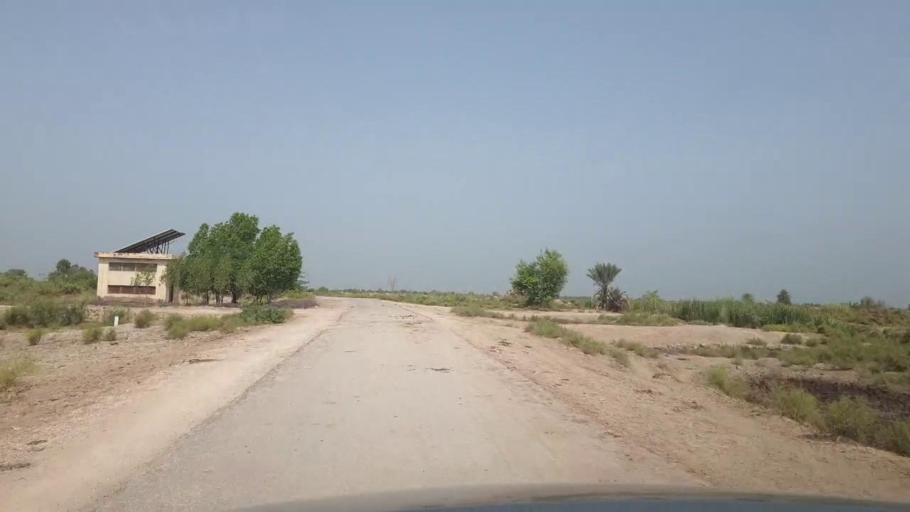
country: PK
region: Sindh
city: Madeji
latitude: 27.8269
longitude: 68.4505
